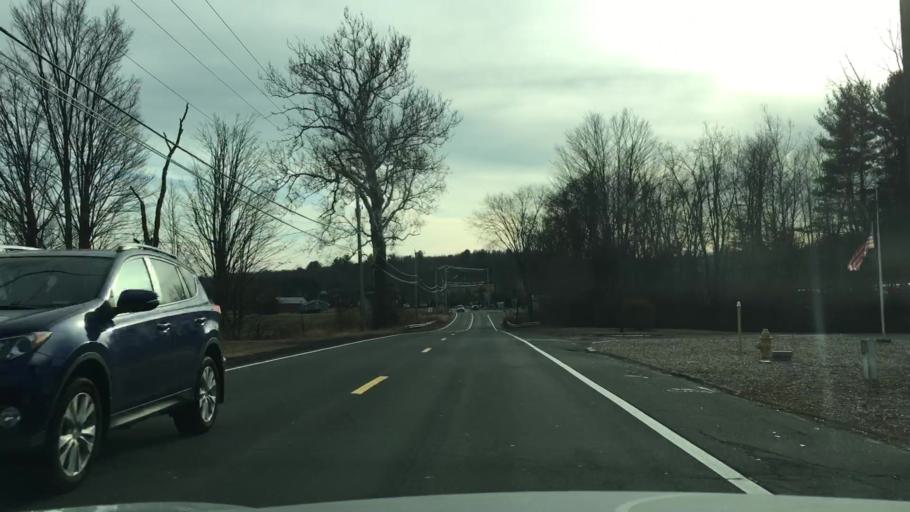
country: US
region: Massachusetts
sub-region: Hampden County
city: Southwick
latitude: 42.0798
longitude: -72.7679
